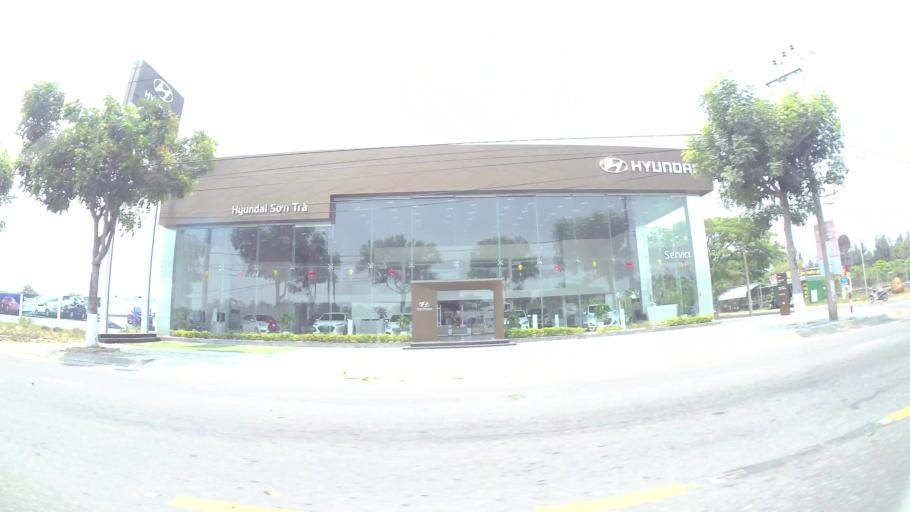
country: VN
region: Da Nang
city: Cam Le
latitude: 15.9941
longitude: 108.2074
